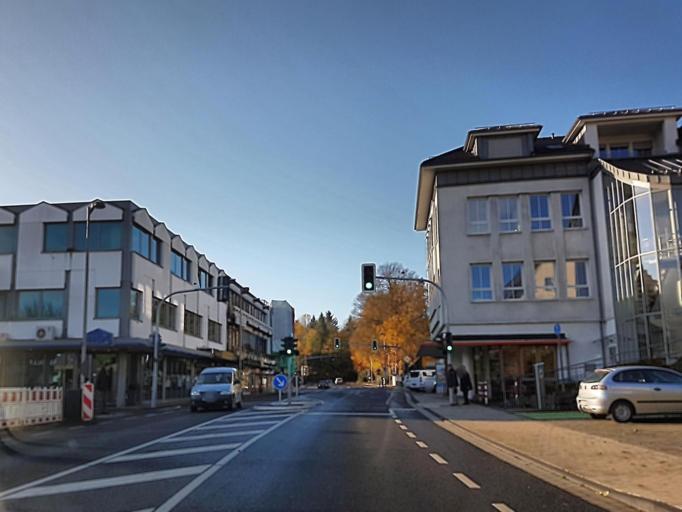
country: DE
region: North Rhine-Westphalia
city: Meinerzhagen
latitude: 51.1081
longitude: 7.6392
